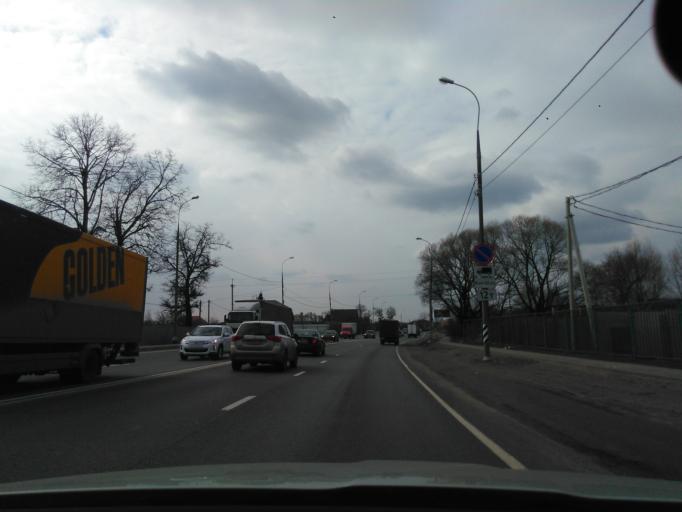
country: RU
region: Moskovskaya
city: Marfino
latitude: 56.0099
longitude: 37.5447
